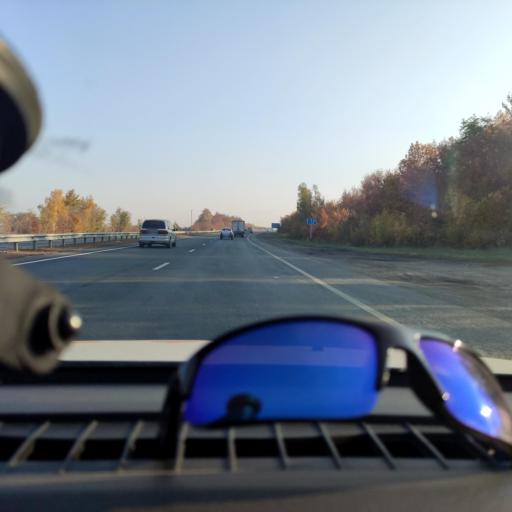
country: RU
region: Samara
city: Novokuybyshevsk
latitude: 53.0000
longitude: 49.9596
